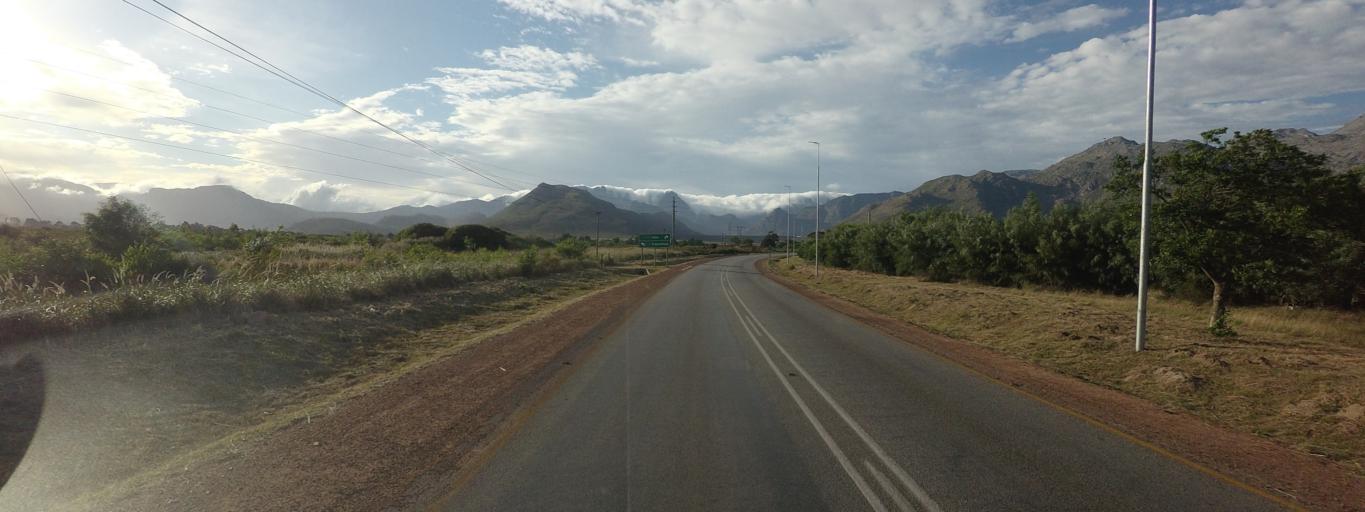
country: ZA
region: Western Cape
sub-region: Cape Winelands District Municipality
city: Paarl
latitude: -33.8722
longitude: 19.0442
